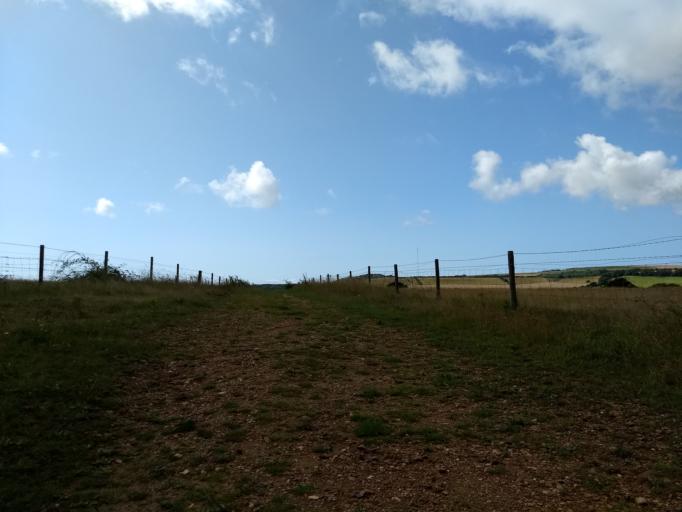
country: GB
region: England
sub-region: Isle of Wight
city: Newport
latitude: 50.6790
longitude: -1.2979
